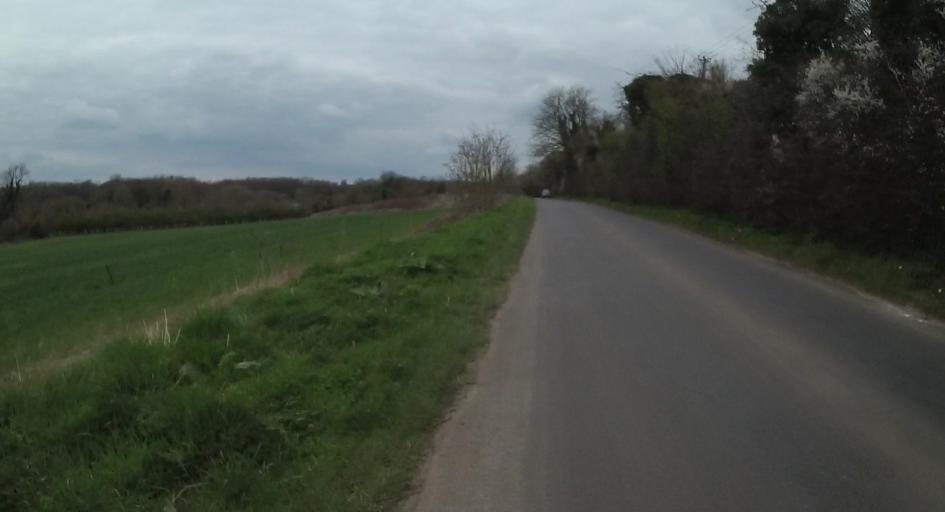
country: GB
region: England
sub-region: Hampshire
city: Odiham
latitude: 51.2432
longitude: -0.9721
